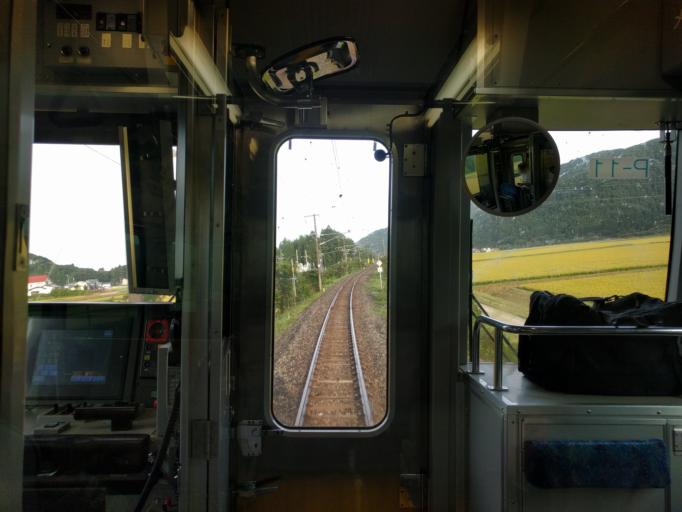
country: JP
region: Fukushima
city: Inawashiro
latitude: 37.4835
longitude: 140.1737
